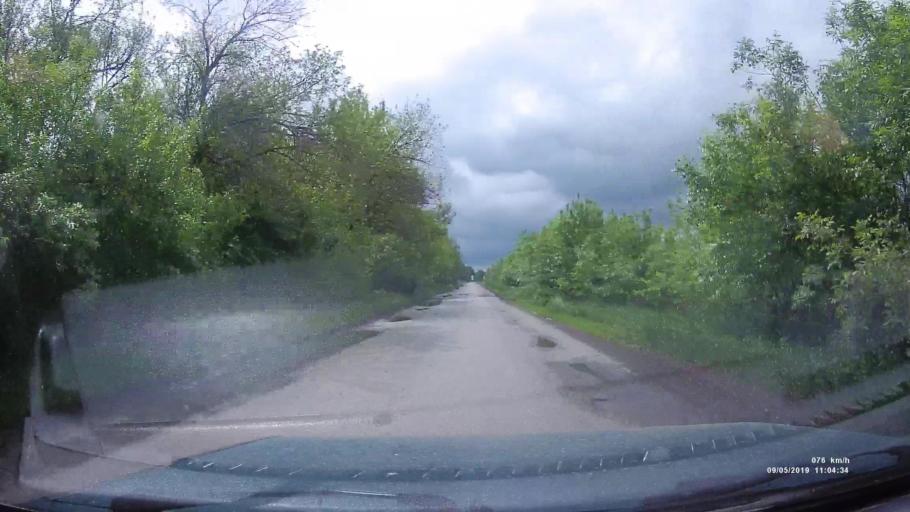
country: RU
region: Krasnodarskiy
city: Kanelovskaya
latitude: 46.8156
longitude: 39.2099
